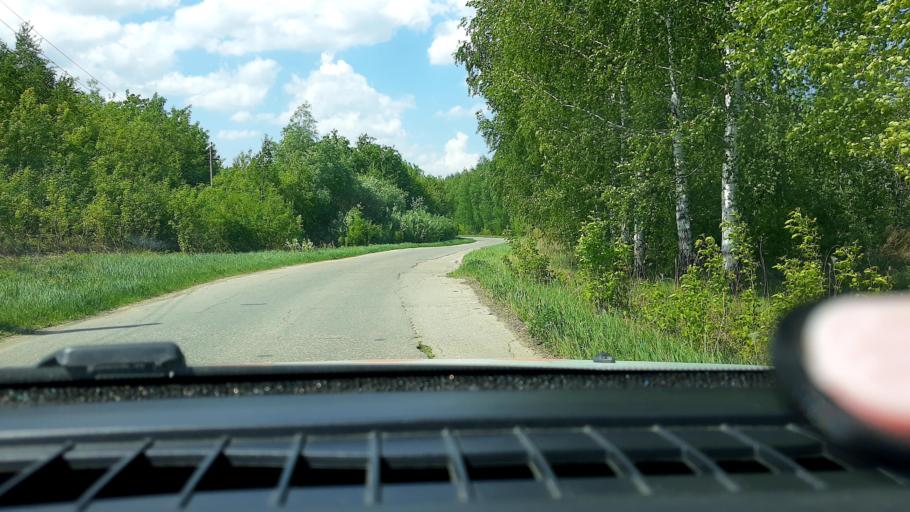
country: RU
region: Nizjnij Novgorod
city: Kstovo
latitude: 56.1469
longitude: 44.1313
